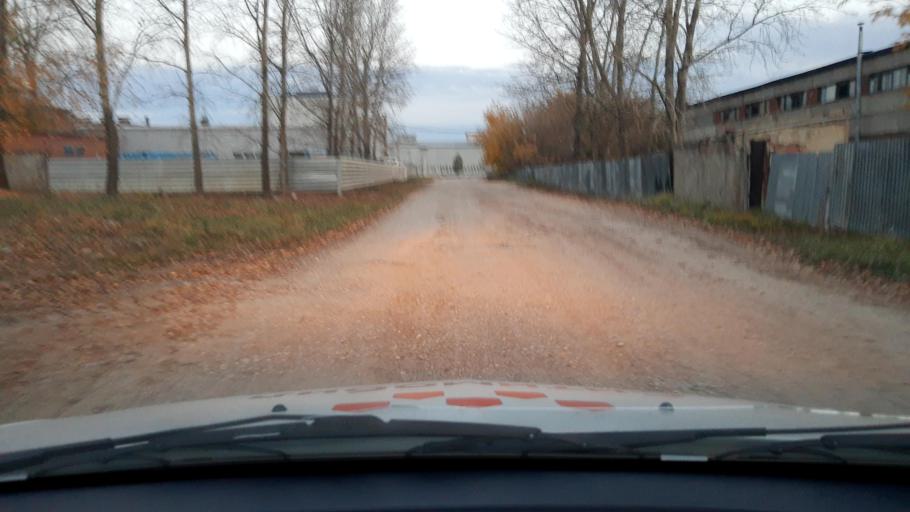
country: RU
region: Bashkortostan
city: Iglino
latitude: 54.7685
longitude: 56.2428
